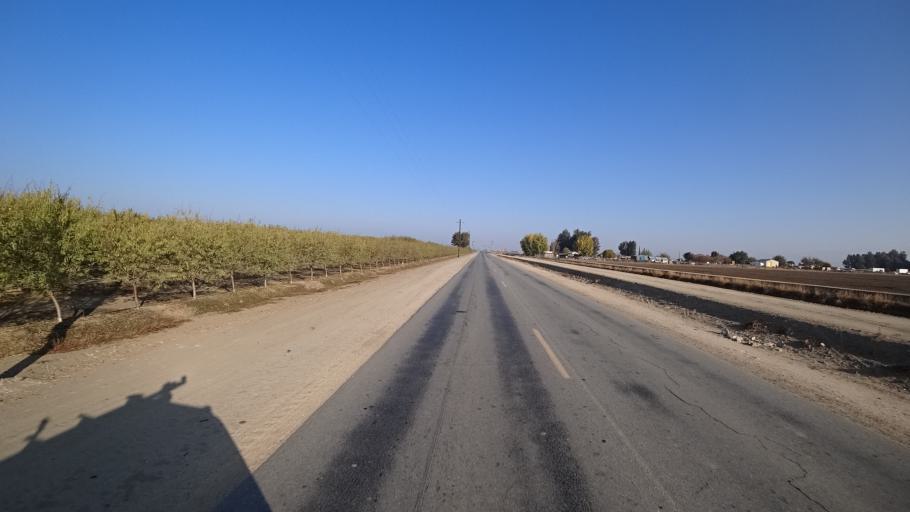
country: US
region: California
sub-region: Kern County
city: Greenfield
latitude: 35.2491
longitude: -118.9853
